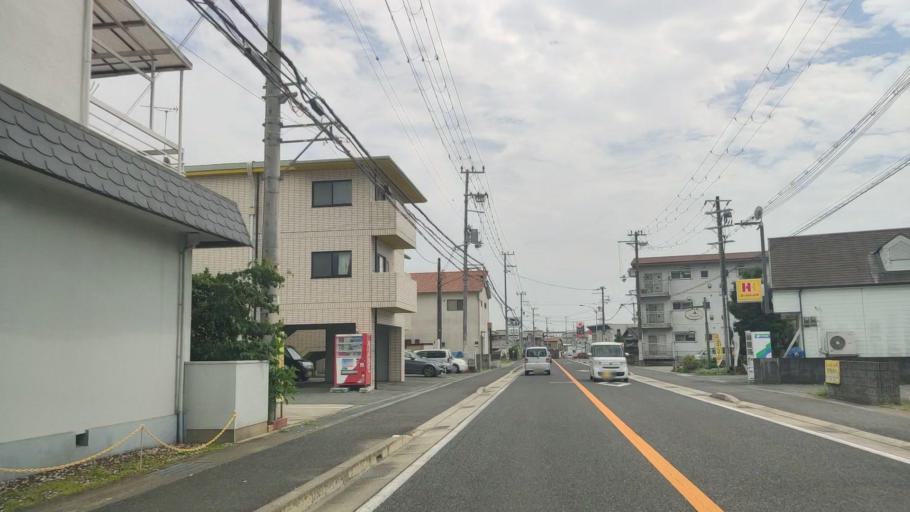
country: JP
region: Hyogo
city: Tatsunocho-tominaga
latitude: 34.8700
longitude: 134.5541
